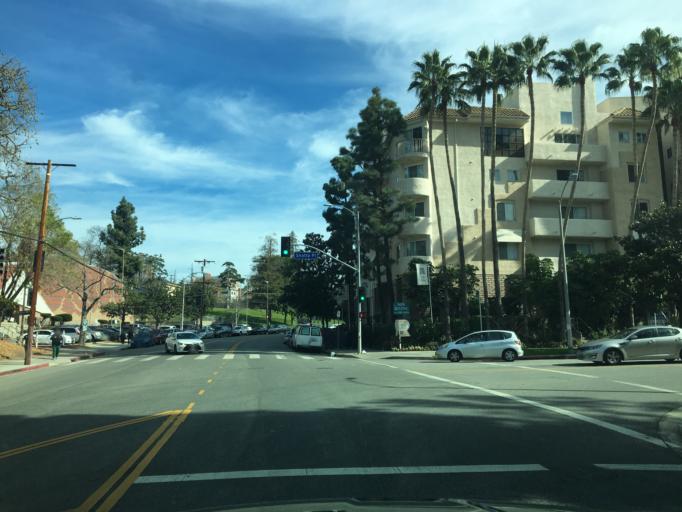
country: US
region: California
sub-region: Los Angeles County
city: Silver Lake
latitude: 34.0669
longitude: -118.2903
